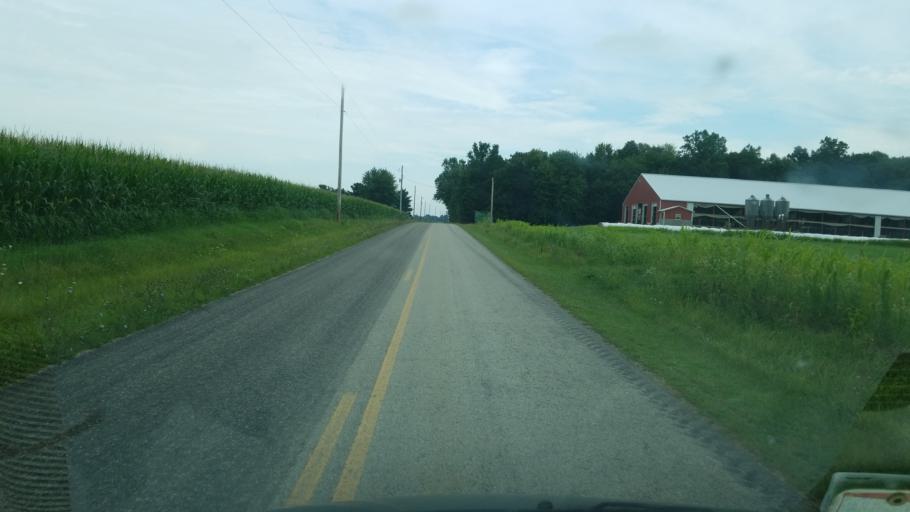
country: US
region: Ohio
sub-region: Seneca County
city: Tiffin
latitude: 40.9972
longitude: -83.0550
